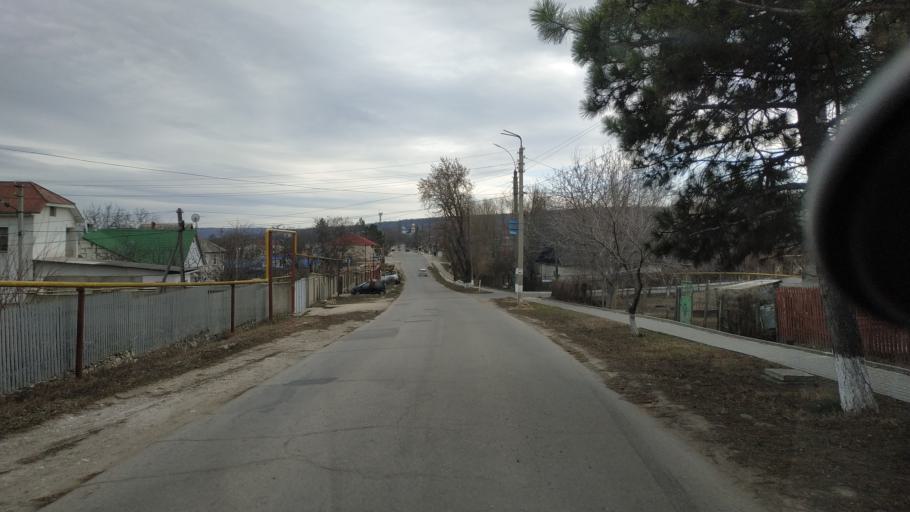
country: MD
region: Chisinau
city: Vadul lui Voda
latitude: 47.0951
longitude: 29.0720
